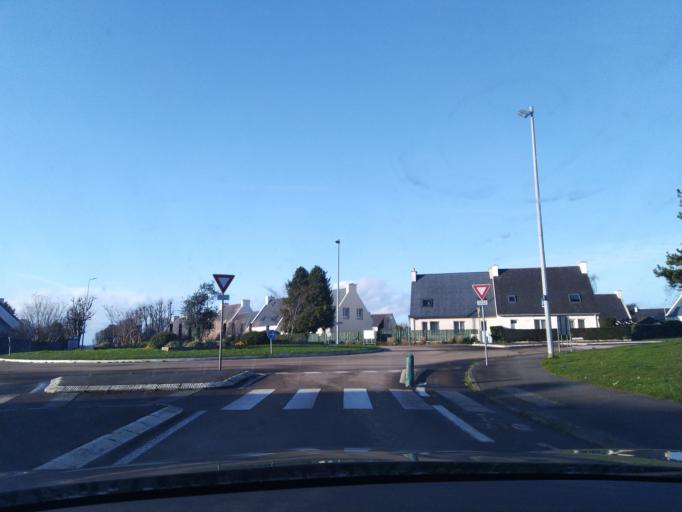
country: FR
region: Brittany
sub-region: Departement du Finistere
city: Morlaix
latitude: 48.5874
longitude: -3.8206
